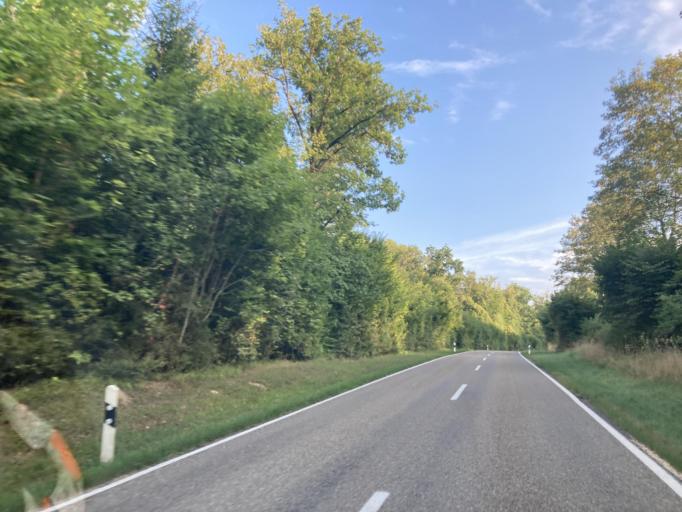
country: DE
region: Bavaria
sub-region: Swabia
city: Medlingen
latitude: 48.5911
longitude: 10.3092
